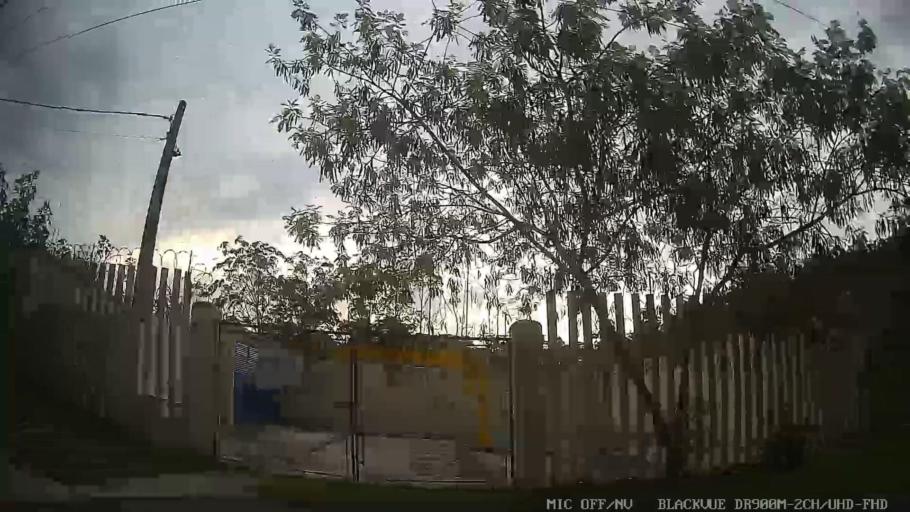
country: BR
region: Sao Paulo
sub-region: Ribeirao Pires
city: Ribeirao Pires
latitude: -23.6997
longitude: -46.4262
